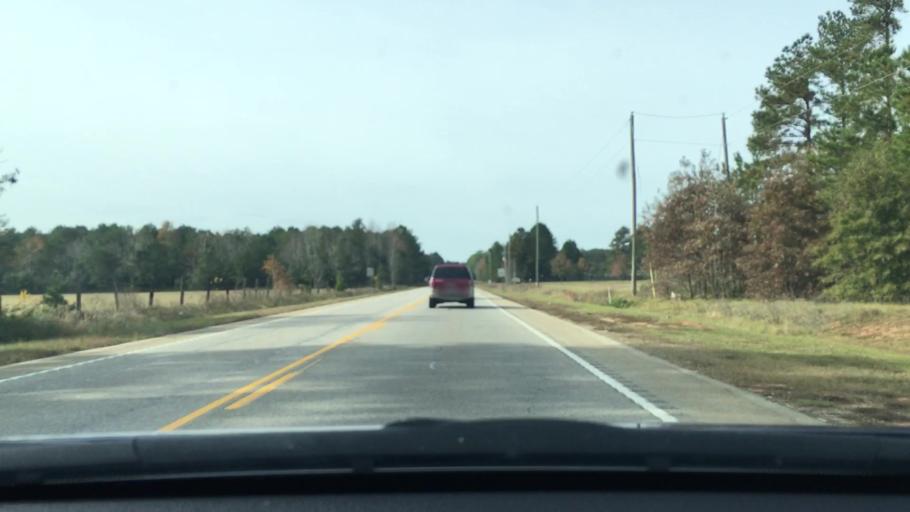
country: US
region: South Carolina
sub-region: Sumter County
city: Cherryvale
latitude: 33.9400
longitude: -80.4800
